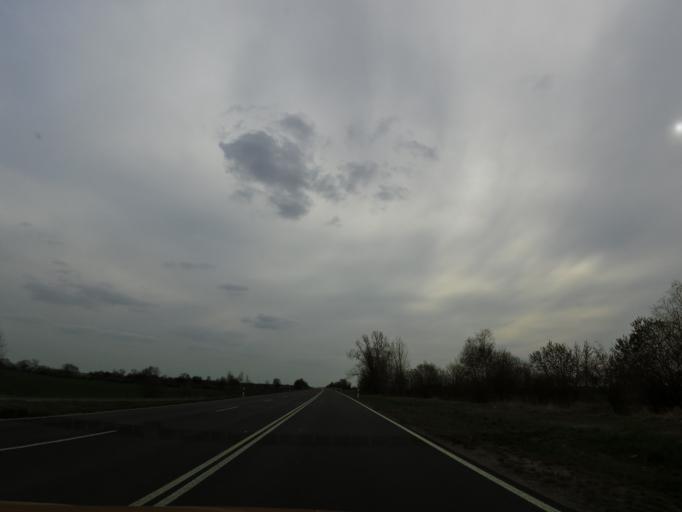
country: DE
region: Brandenburg
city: Beeskow
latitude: 52.1806
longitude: 14.2168
